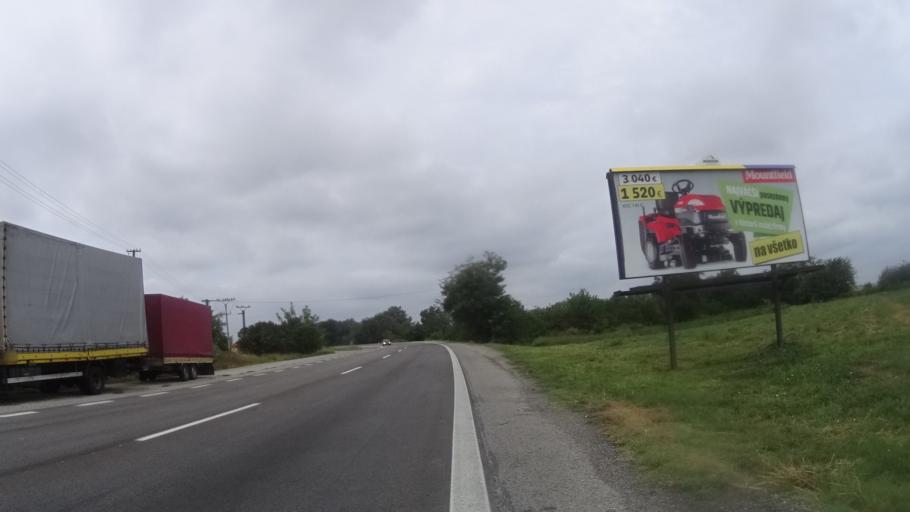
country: HU
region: Komarom-Esztergom
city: Acs
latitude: 47.7656
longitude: 18.0359
